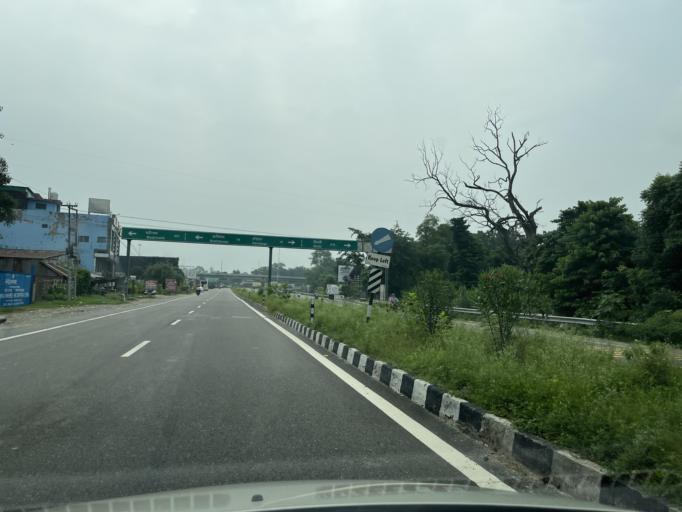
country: IN
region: Uttarakhand
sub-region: Dehradun
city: Raiwala
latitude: 30.0565
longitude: 78.2170
